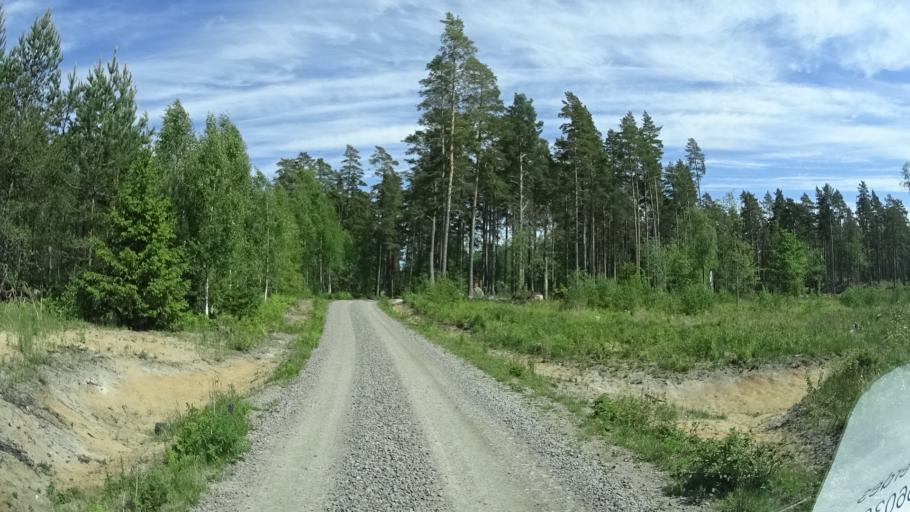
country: SE
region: OEstergoetland
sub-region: Norrkopings Kommun
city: Svartinge
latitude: 58.7708
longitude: 15.9644
